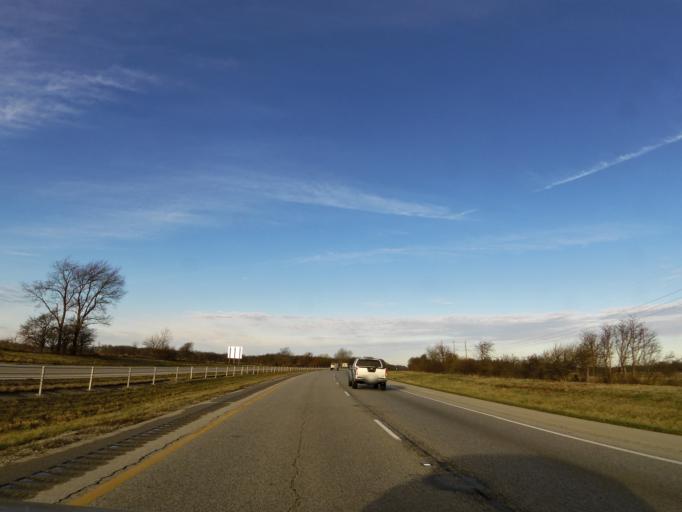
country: US
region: Illinois
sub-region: Vermilion County
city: Tilton
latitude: 40.1050
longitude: -87.6744
